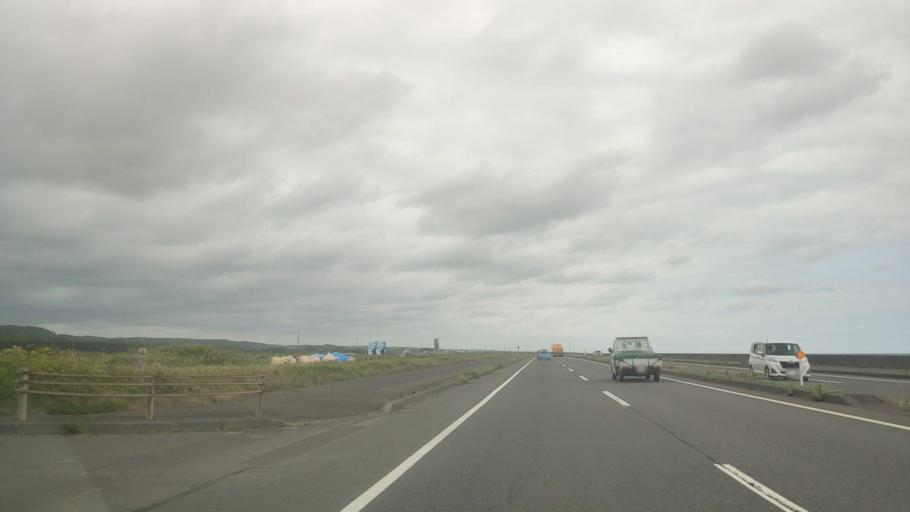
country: JP
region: Hokkaido
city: Shiraoi
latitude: 42.5552
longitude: 141.3745
